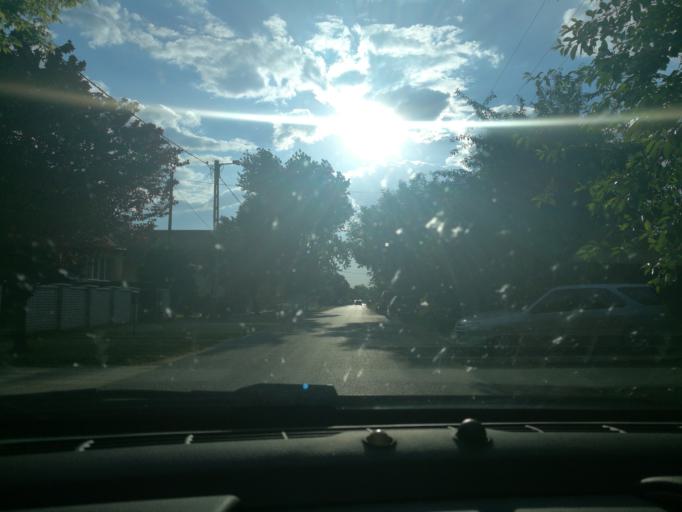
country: HU
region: Szabolcs-Szatmar-Bereg
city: Nyirpazony
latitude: 47.9458
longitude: 21.7827
